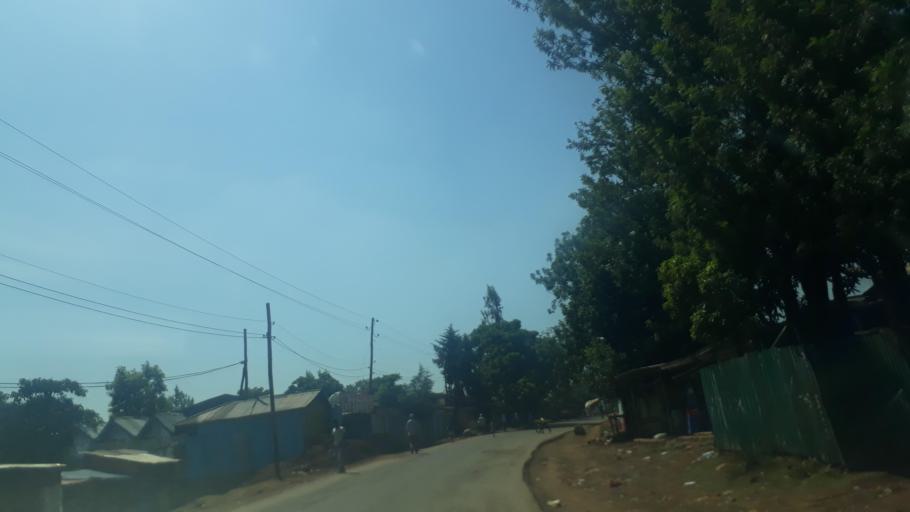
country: ET
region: Oromiya
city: Agaro
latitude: 7.7888
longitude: 36.7279
